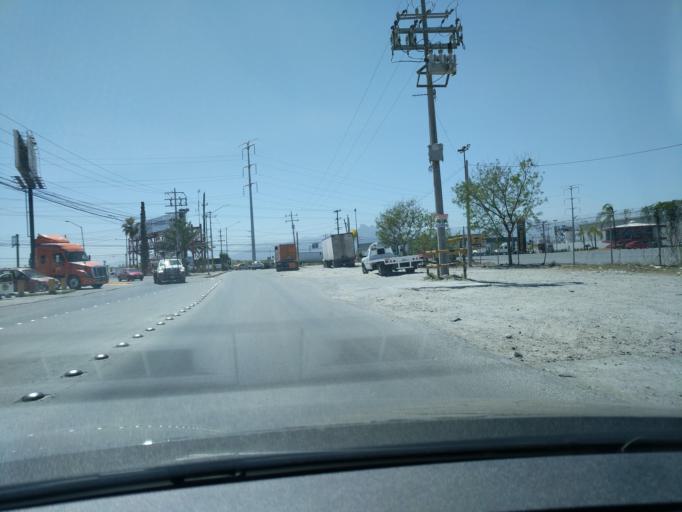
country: MX
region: Nuevo Leon
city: Apodaca
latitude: 25.7859
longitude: -100.1595
